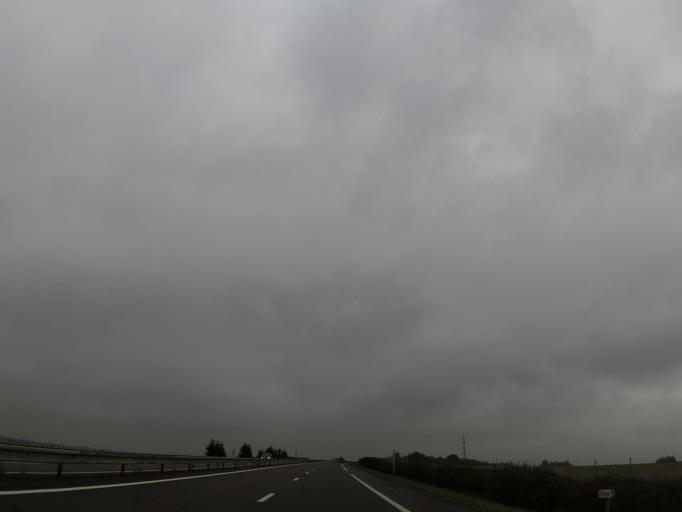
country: FR
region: Champagne-Ardenne
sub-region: Departement de la Marne
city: Saint-Memmie
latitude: 49.0356
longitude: 4.4263
